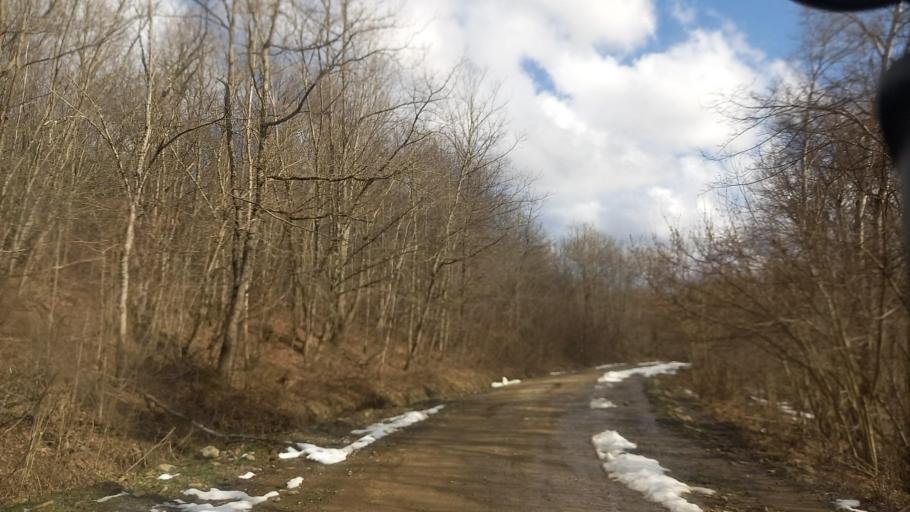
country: RU
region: Krasnodarskiy
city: Smolenskaya
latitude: 44.6018
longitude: 38.8732
